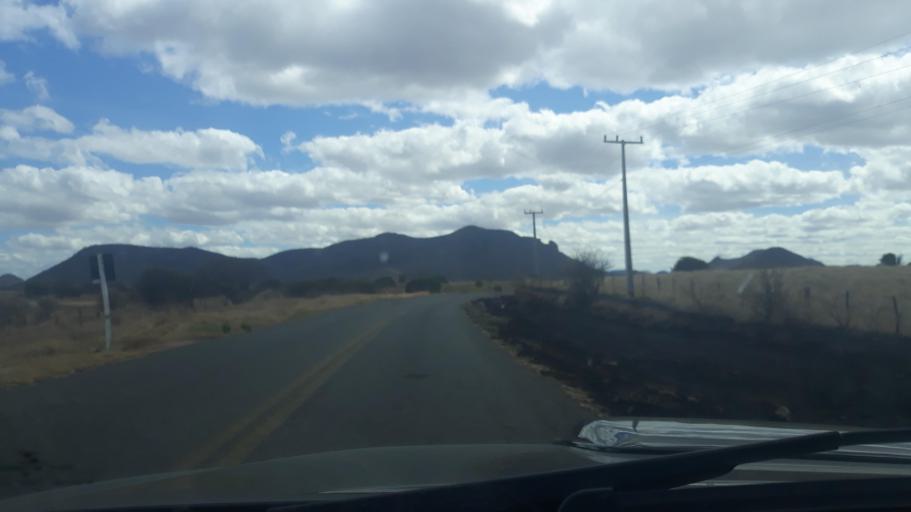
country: BR
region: Bahia
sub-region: Guanambi
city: Guanambi
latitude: -14.1597
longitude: -42.8174
